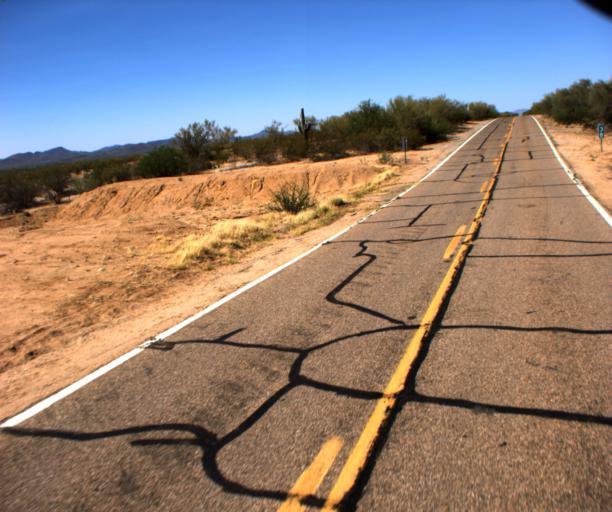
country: US
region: Arizona
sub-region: Pima County
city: Three Points
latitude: 31.9819
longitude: -111.3745
